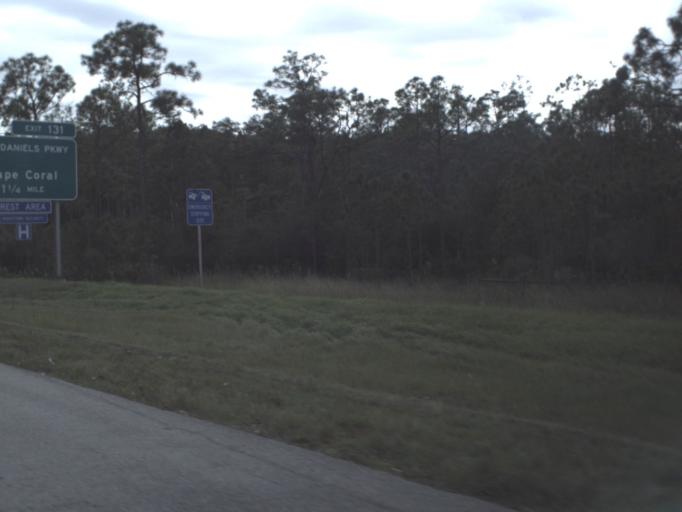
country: US
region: Florida
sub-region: Lee County
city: Gateway
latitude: 26.5688
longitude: -81.7937
